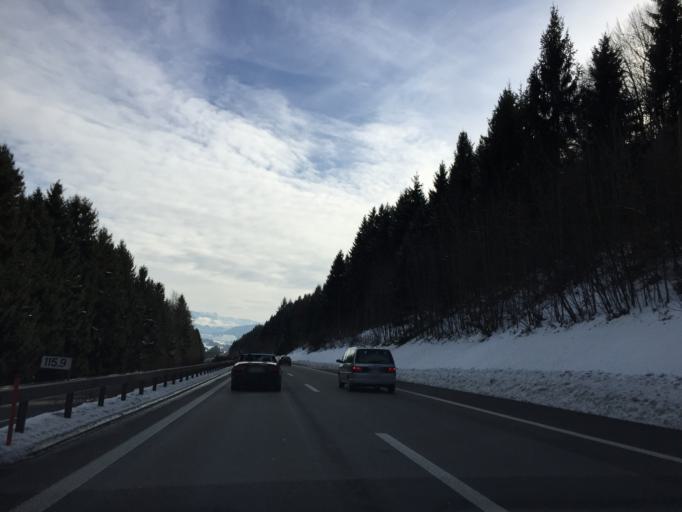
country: CH
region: Zurich
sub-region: Bezirk Horgen
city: Horgen / Scheller-Stockerstrasse
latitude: 47.2596
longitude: 8.5809
